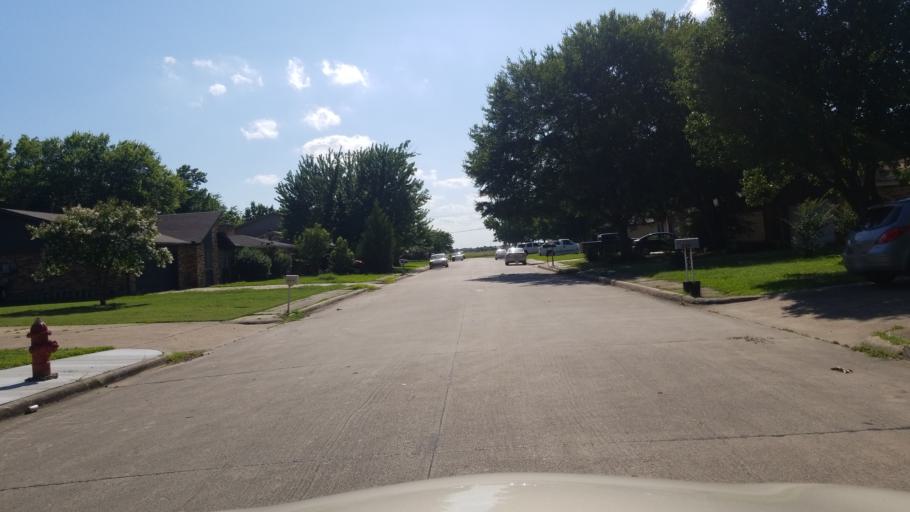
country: US
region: Texas
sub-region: Dallas County
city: Grand Prairie
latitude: 32.6867
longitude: -97.0165
